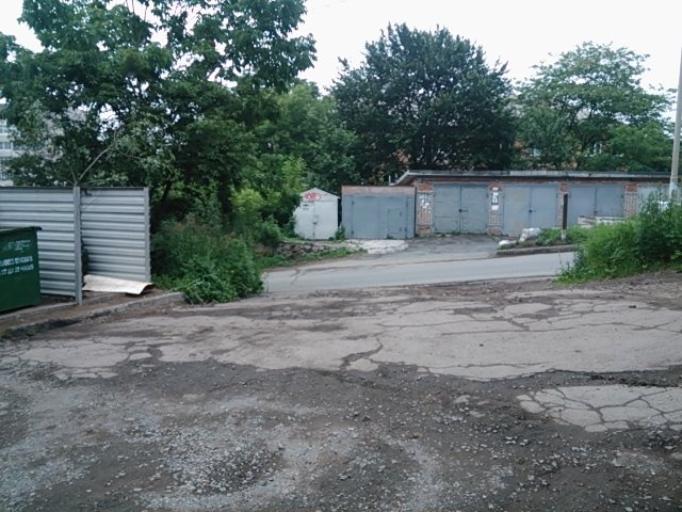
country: RU
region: Primorskiy
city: Vladivostok
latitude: 43.0950
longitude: 131.9590
